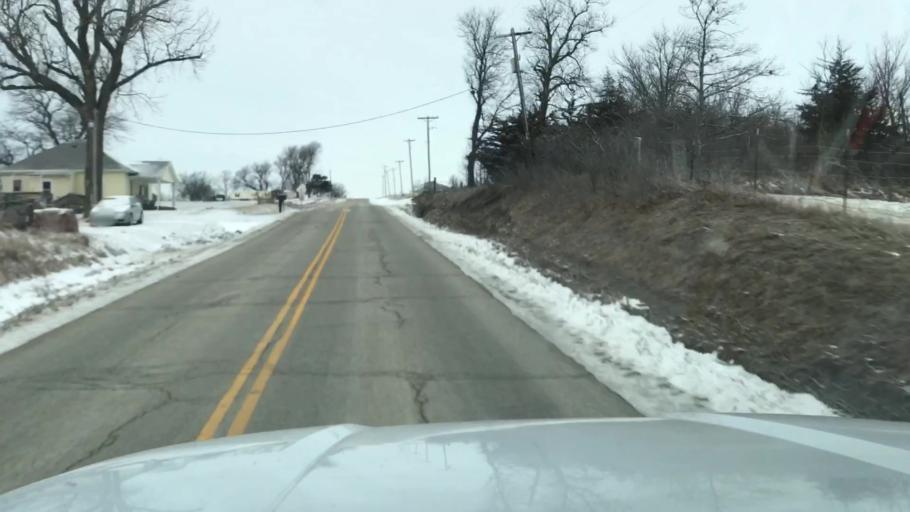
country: US
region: Missouri
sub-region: Andrew County
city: Savannah
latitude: 40.0247
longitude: -94.9206
